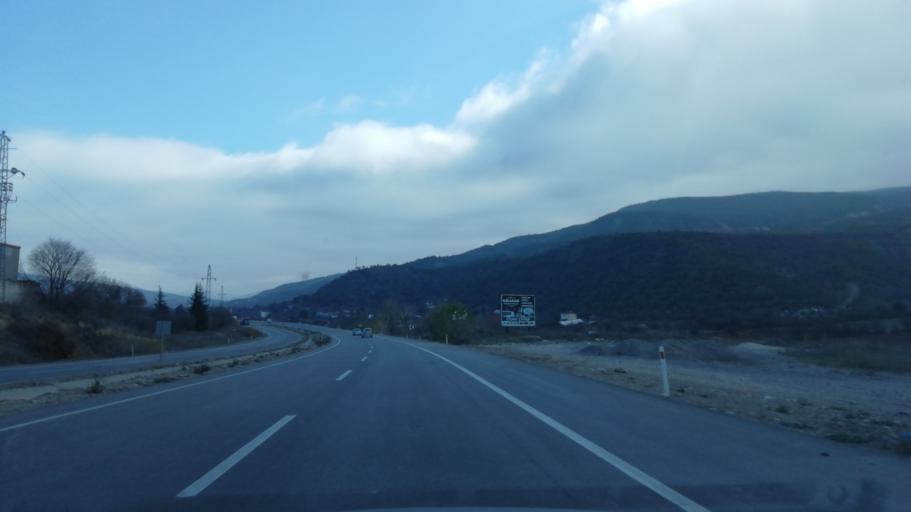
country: TR
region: Karabuk
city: Safranbolu
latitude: 41.2175
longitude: 32.7302
